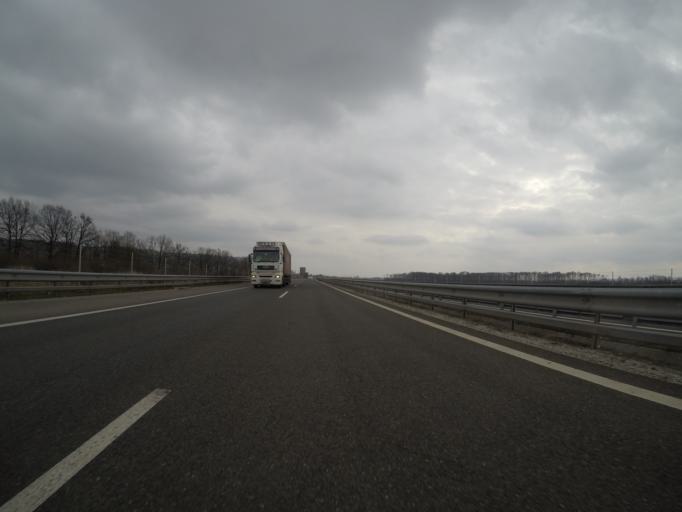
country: SI
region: Lendava-Lendva
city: Lendava
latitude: 46.5814
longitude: 16.4354
